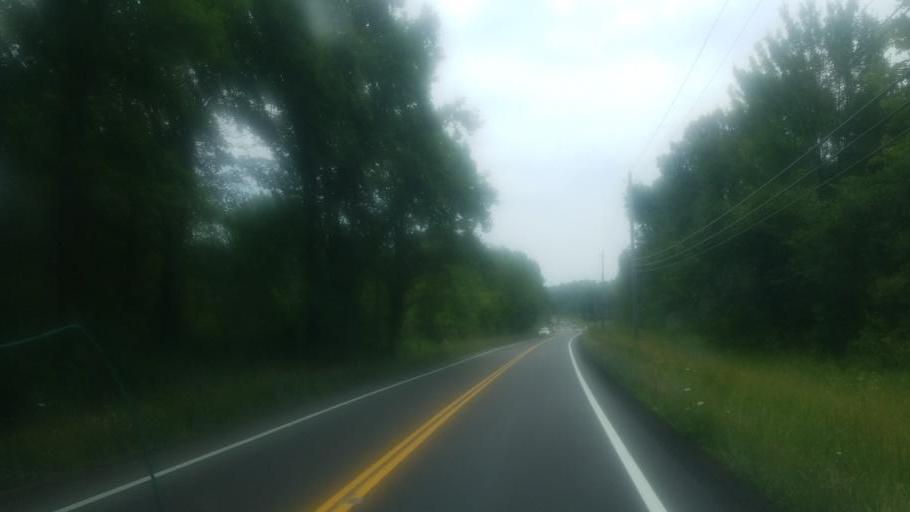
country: US
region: Ohio
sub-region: Columbiana County
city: Columbiana
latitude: 40.9440
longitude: -80.6876
